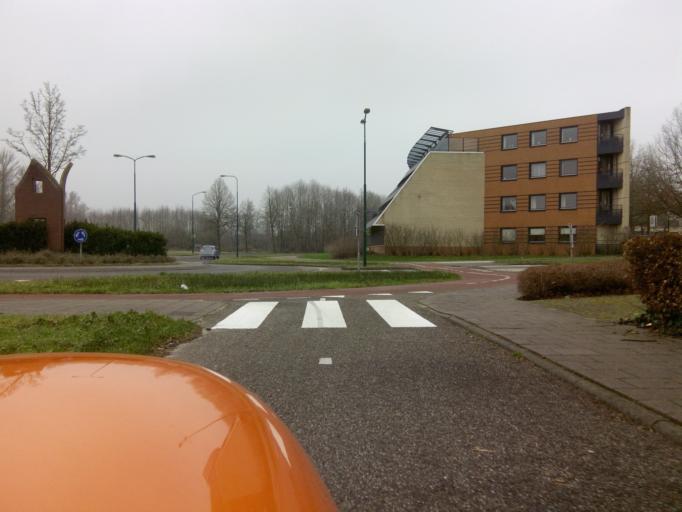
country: NL
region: Utrecht
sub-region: Gemeente Leusden
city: Leusden
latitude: 52.1277
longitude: 5.4279
